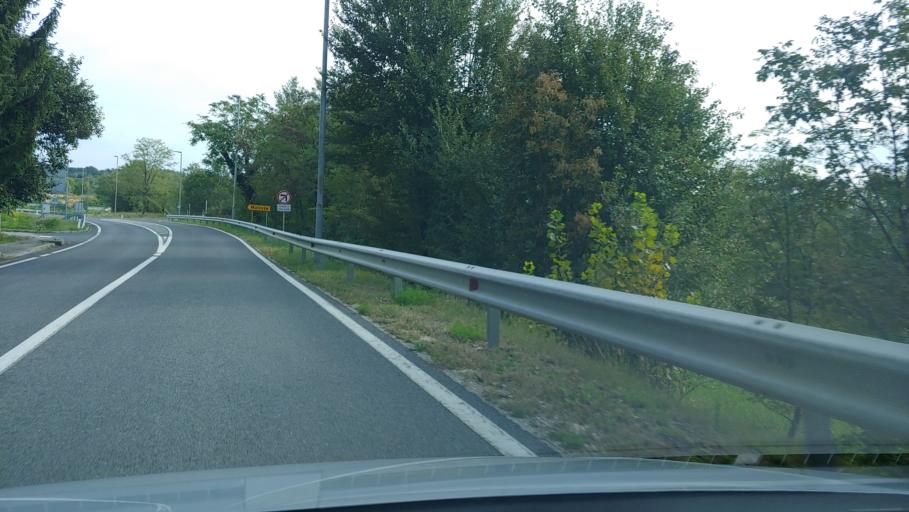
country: SI
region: Nova Gorica
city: Sempas
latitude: 45.8976
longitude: 13.7854
